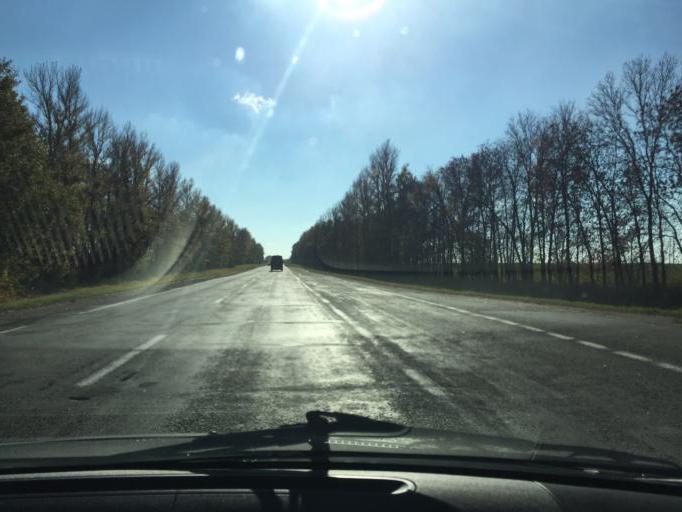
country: BY
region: Minsk
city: Salihorsk
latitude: 52.9012
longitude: 27.4760
